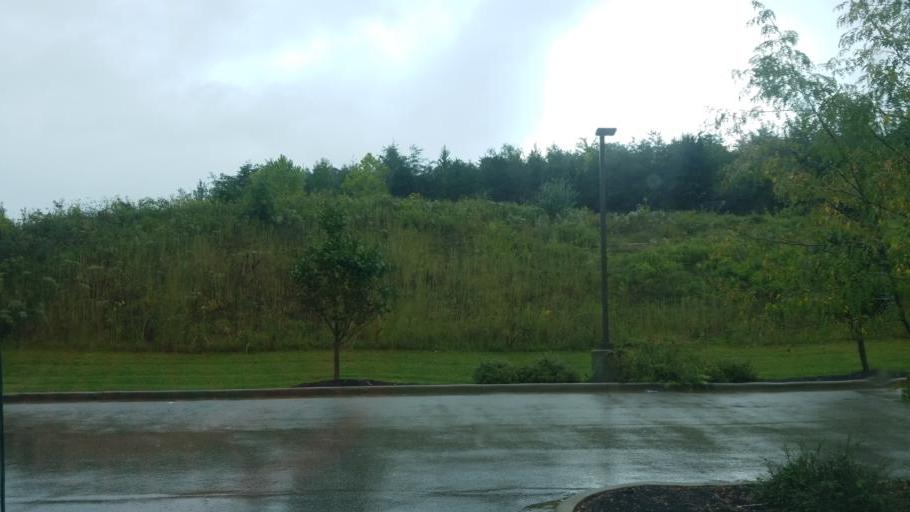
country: US
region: Kentucky
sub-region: Rowan County
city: Morehead
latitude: 38.2014
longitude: -83.4752
